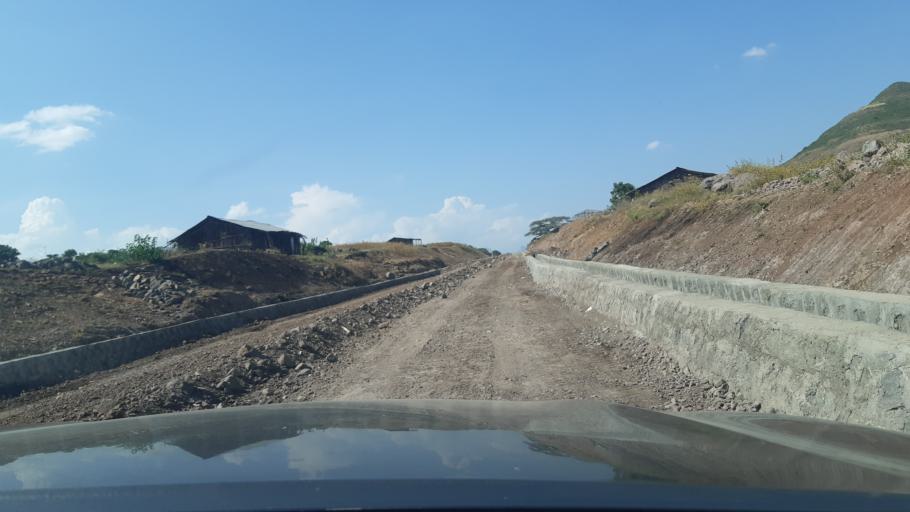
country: ET
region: Amhara
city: Dabat
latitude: 13.1603
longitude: 37.6075
